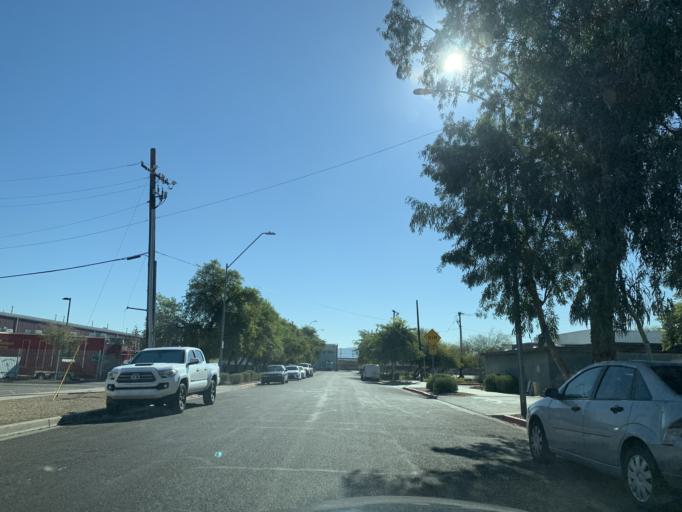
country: US
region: Arizona
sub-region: Maricopa County
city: Phoenix
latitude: 33.4466
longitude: -112.0590
